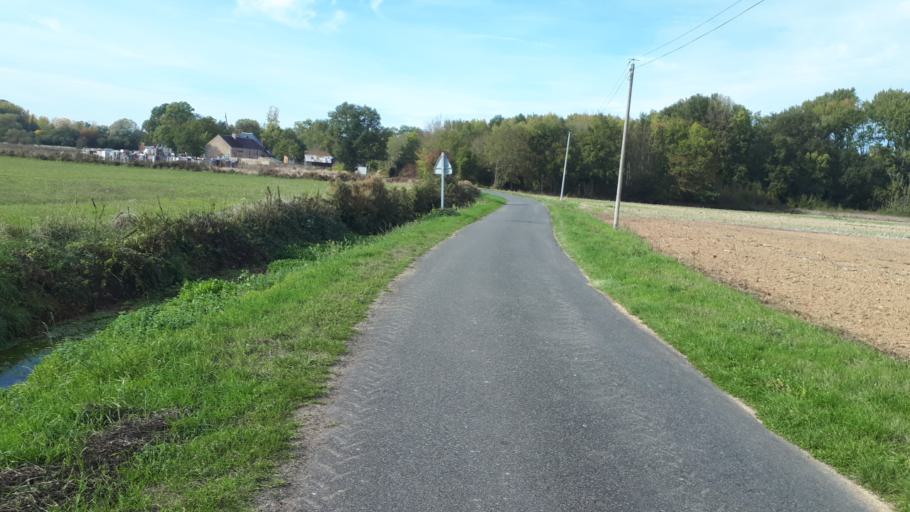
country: FR
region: Centre
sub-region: Departement du Loir-et-Cher
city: Villiers-sur-Loir
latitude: 47.7693
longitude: 0.9554
